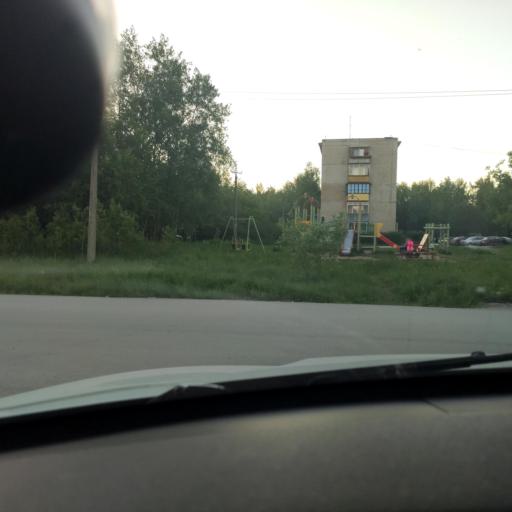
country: RU
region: Perm
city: Polazna
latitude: 58.1448
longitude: 56.4422
